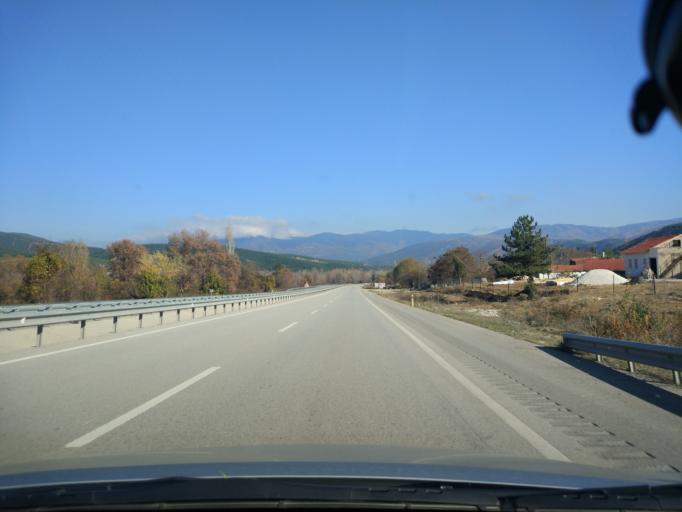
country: TR
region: Karabuk
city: Eskipazar
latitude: 40.9891
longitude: 32.5696
